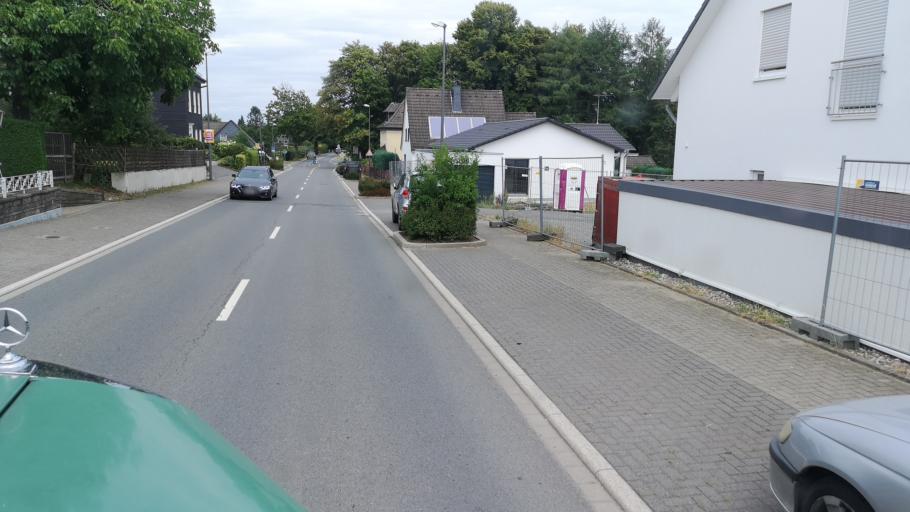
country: DE
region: North Rhine-Westphalia
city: Wermelskirchen
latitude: 51.1035
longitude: 7.2196
